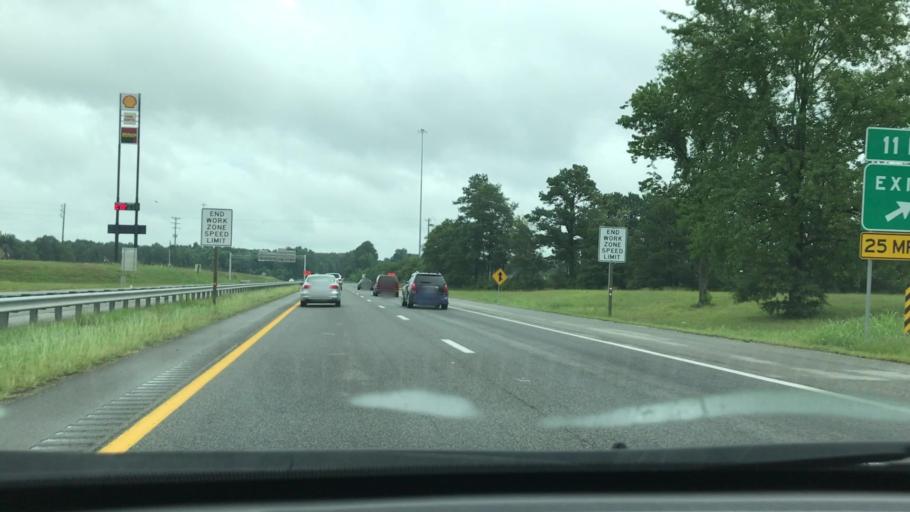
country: US
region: Virginia
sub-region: City of Emporia
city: Emporia
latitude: 36.7032
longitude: -77.5491
